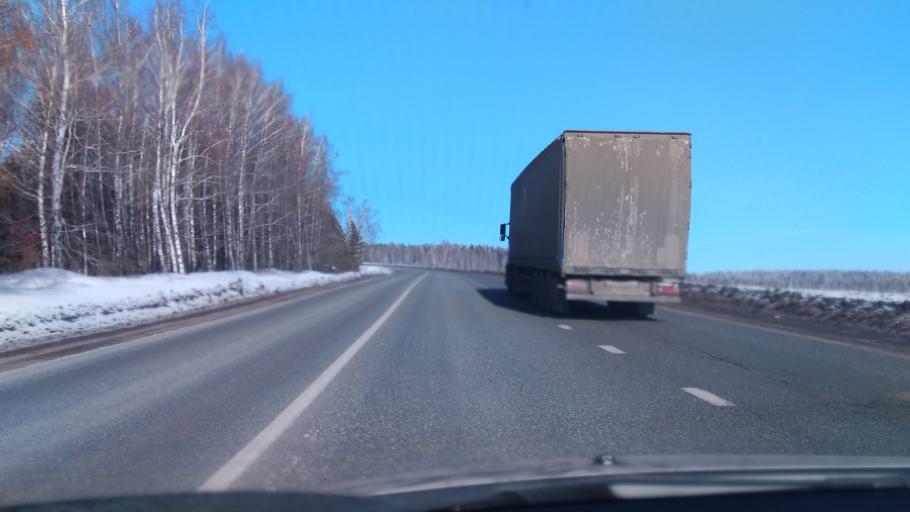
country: RU
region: Perm
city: Suksun
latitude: 57.0781
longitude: 57.4086
